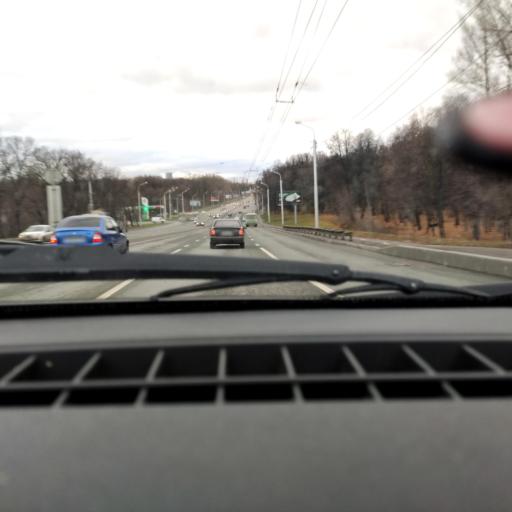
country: RU
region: Bashkortostan
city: Ufa
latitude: 54.8055
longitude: 56.0486
